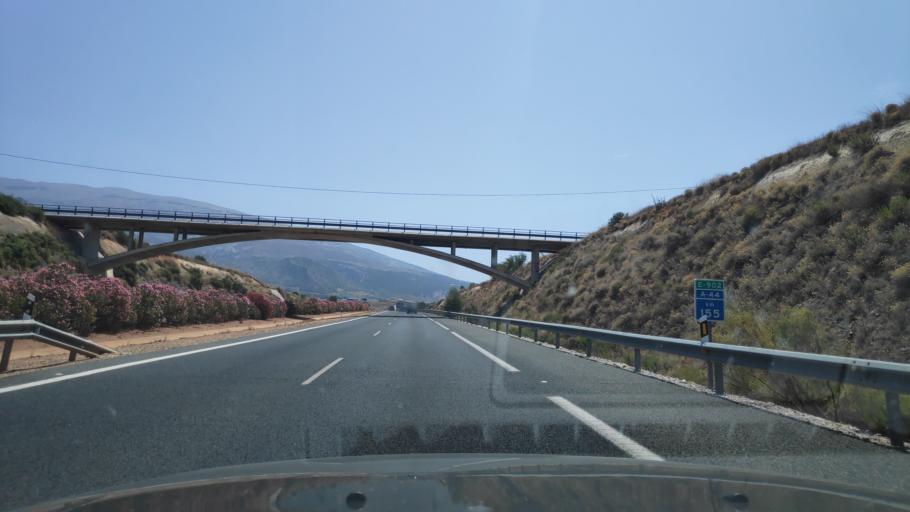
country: ES
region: Andalusia
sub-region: Provincia de Granada
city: Durcal
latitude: 36.9828
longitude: -3.5804
